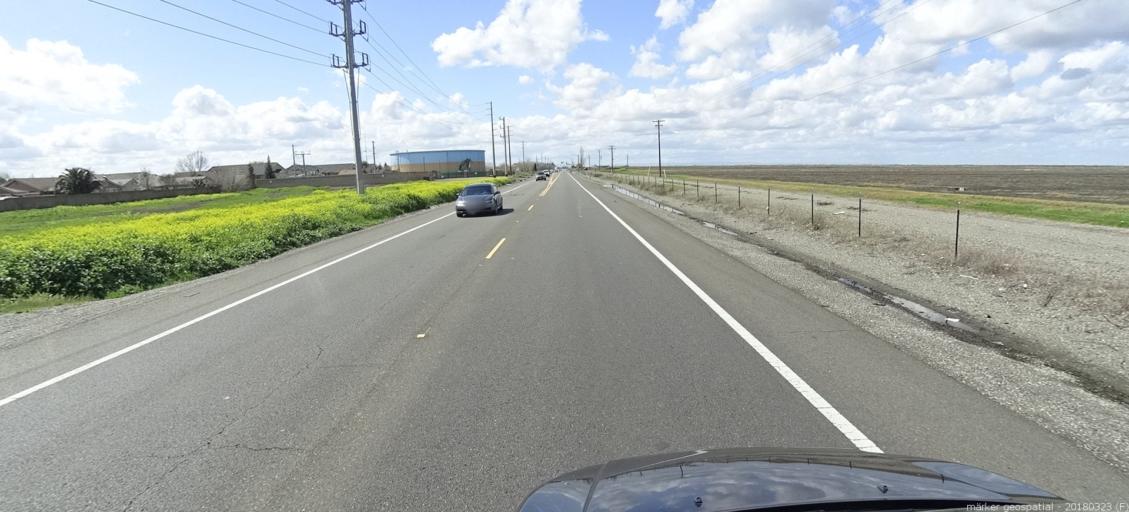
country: US
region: California
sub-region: Sacramento County
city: Elverta
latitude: 38.6853
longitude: -121.5036
